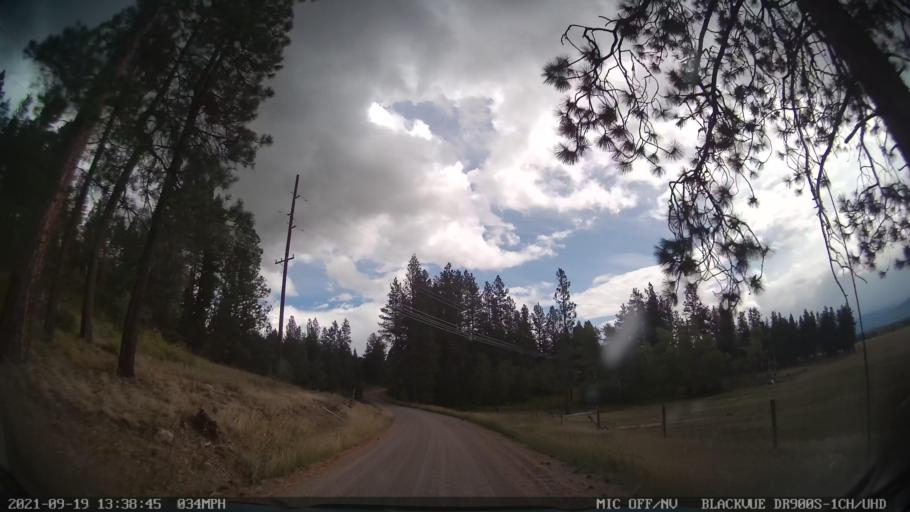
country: US
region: Montana
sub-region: Missoula County
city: Seeley Lake
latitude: 47.1026
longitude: -113.2688
